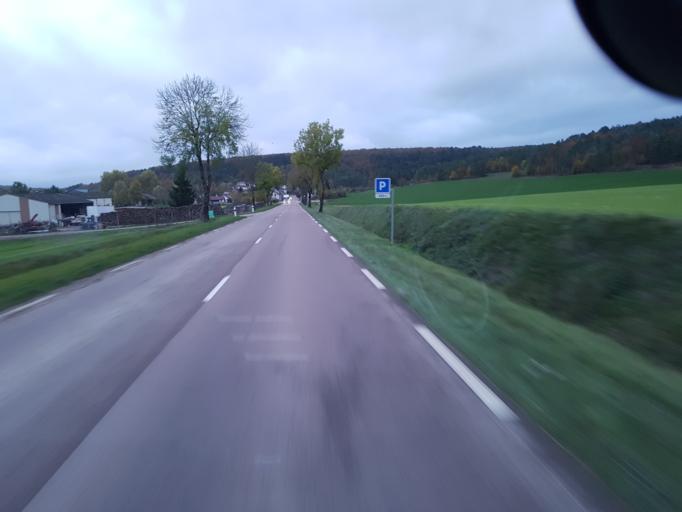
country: FR
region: Champagne-Ardenne
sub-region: Departement de l'Aube
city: Mussy-sur-Seine
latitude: 47.9905
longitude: 4.4840
